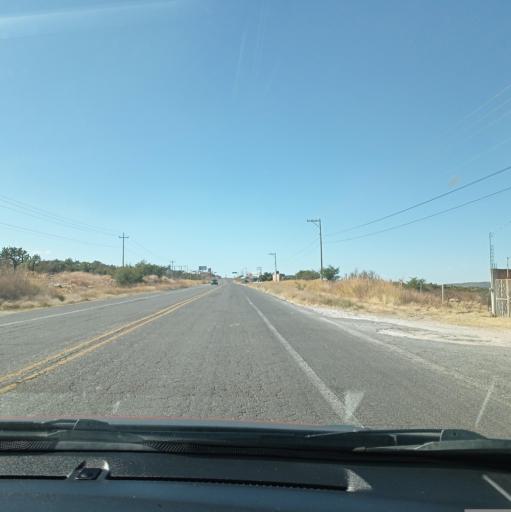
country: MX
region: Jalisco
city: San Miguel el Alto
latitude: 21.0132
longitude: -102.3170
